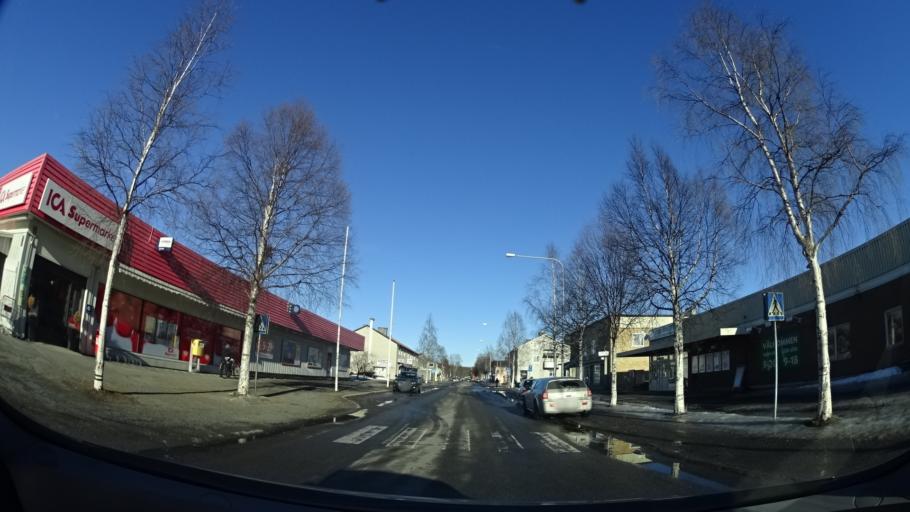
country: SE
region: Vaesterbotten
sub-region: Skelleftea Kommun
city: Byske
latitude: 64.9539
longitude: 21.2024
